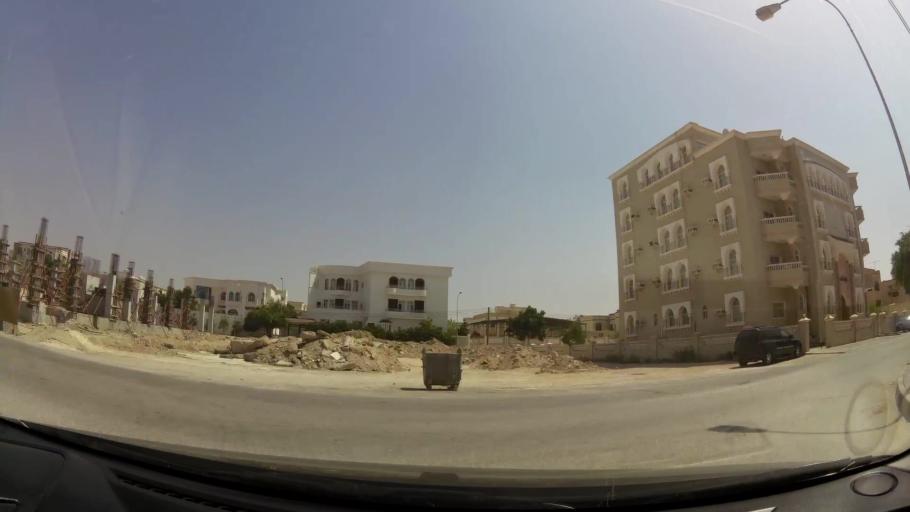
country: OM
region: Zufar
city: Salalah
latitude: 17.0212
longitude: 54.1080
